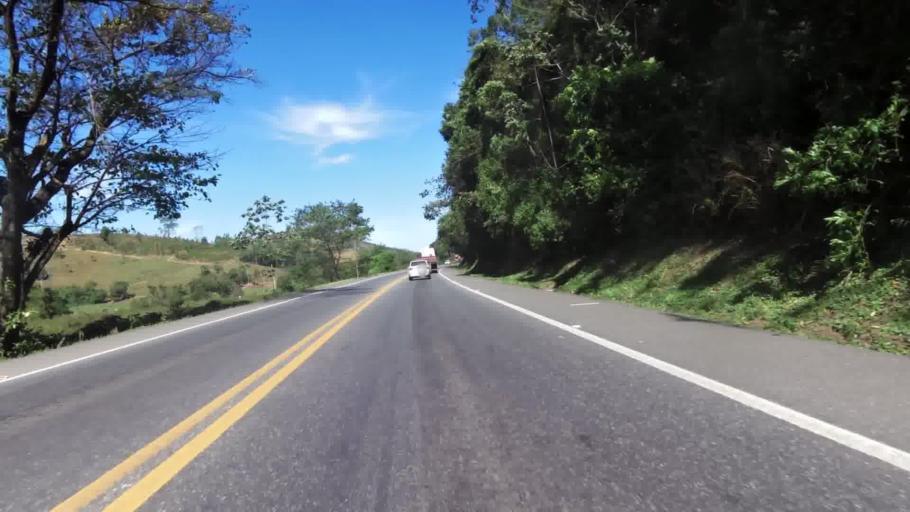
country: BR
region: Espirito Santo
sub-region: Iconha
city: Iconha
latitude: -20.8176
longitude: -40.8432
